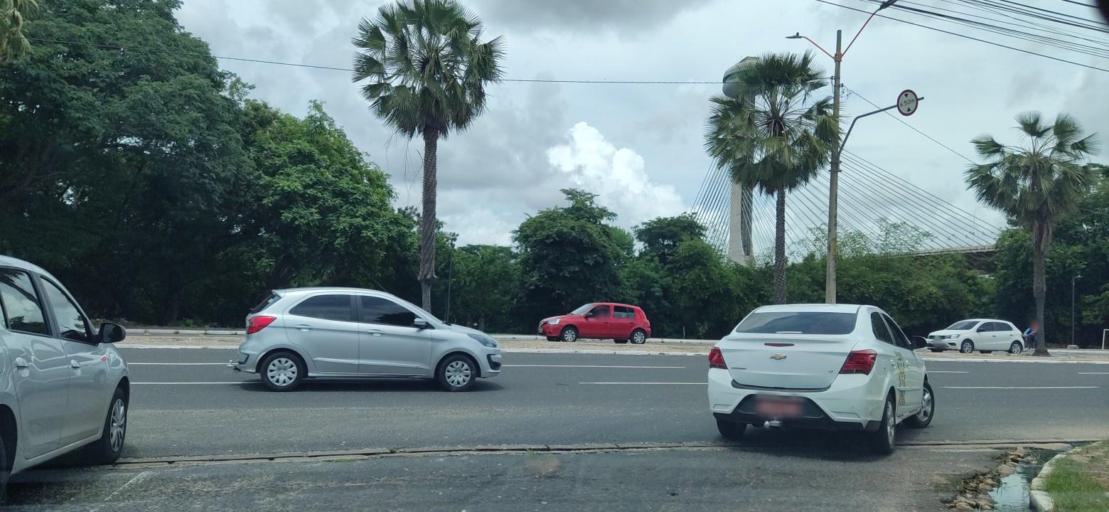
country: BR
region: Piaui
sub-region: Teresina
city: Teresina
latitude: -5.0700
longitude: -42.8052
